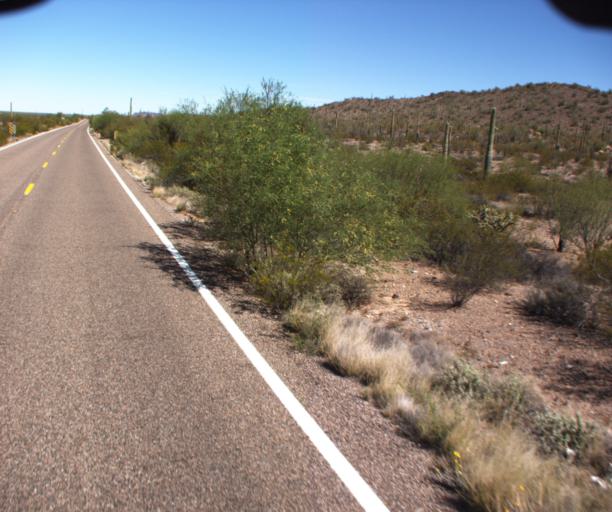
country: MX
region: Sonora
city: Sonoyta
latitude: 32.0031
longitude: -112.8060
